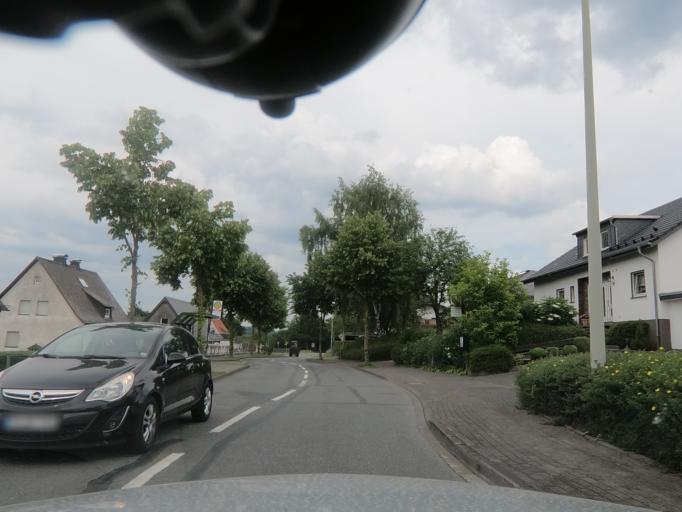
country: DE
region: North Rhine-Westphalia
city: Warstein
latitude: 51.4558
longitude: 8.3842
